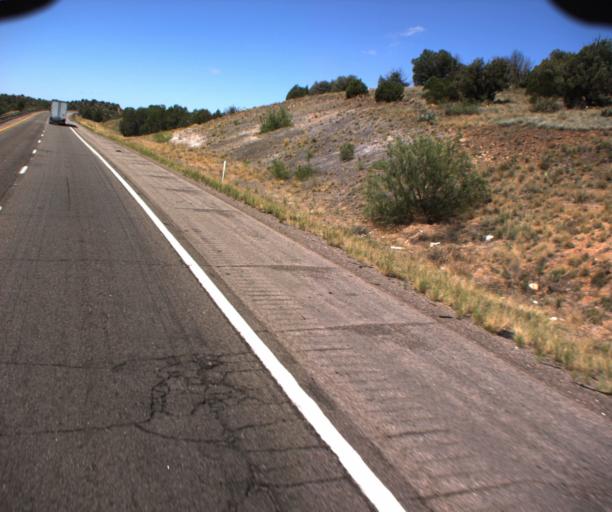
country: US
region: Arizona
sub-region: Mohave County
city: Peach Springs
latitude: 35.1837
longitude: -113.4692
